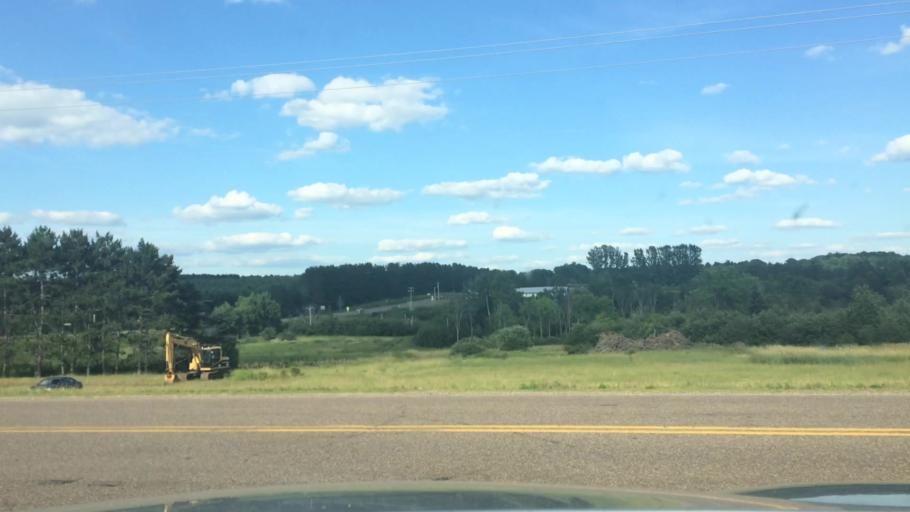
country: US
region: Wisconsin
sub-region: Lincoln County
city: Merrill
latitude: 45.1766
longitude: -89.6418
